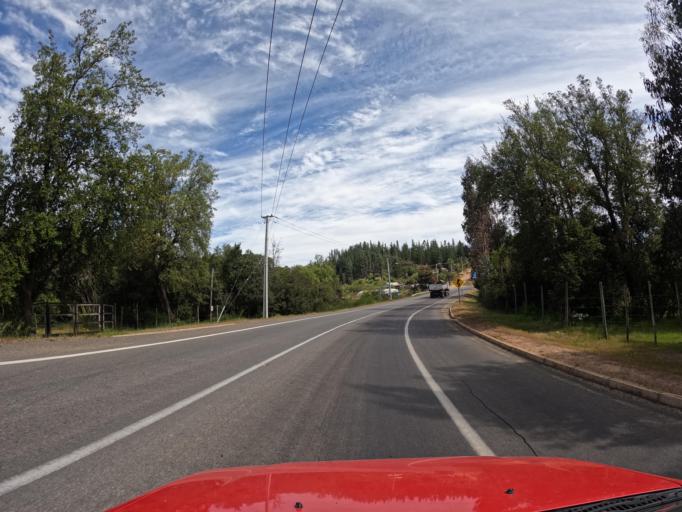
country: CL
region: Maule
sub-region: Provincia de Talca
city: Talca
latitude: -35.1703
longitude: -71.9729
